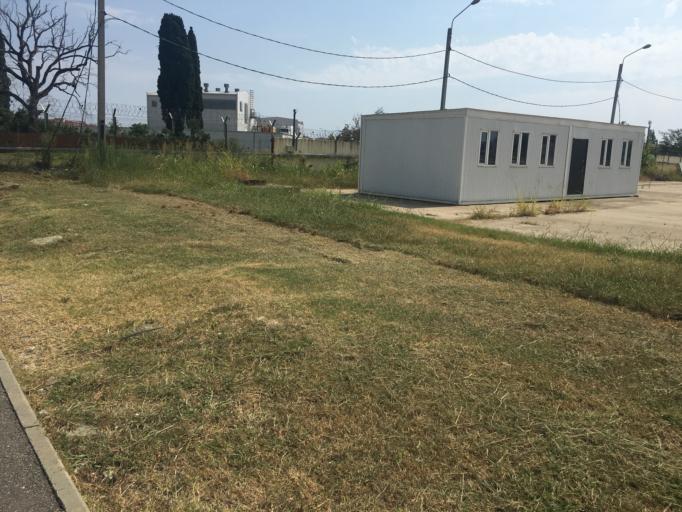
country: RU
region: Krasnodarskiy
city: Vysokoye
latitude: 43.3963
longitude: 39.9873
